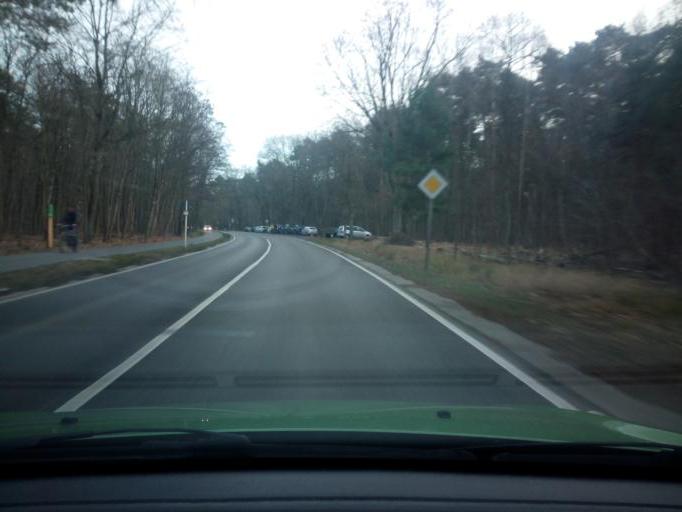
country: DE
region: Berlin
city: Friedrichshagen
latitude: 52.4256
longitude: 13.6224
